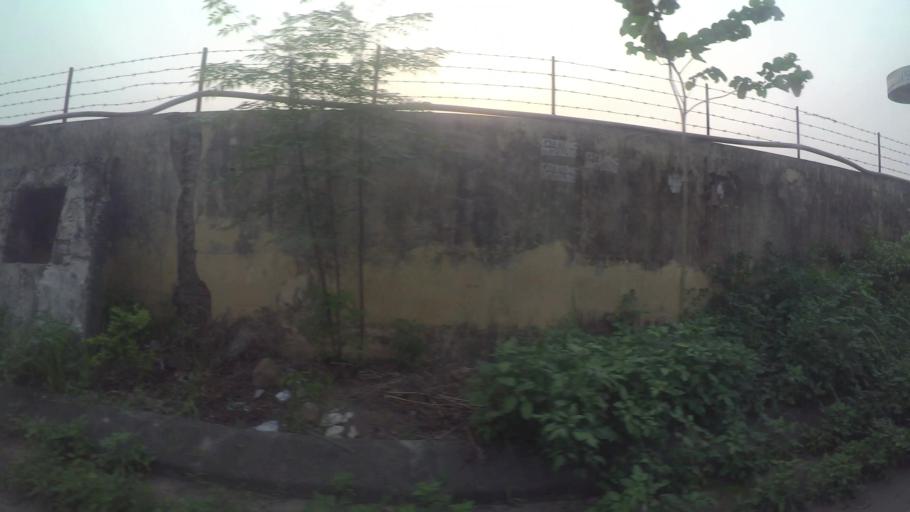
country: VN
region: Ha Noi
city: Cau Dien
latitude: 21.0013
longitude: 105.7274
